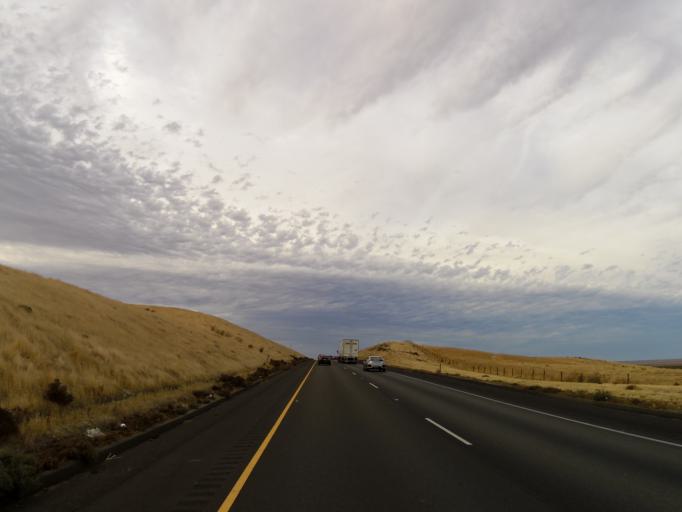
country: US
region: California
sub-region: Kings County
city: Kettleman City
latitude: 35.9966
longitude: -119.9744
